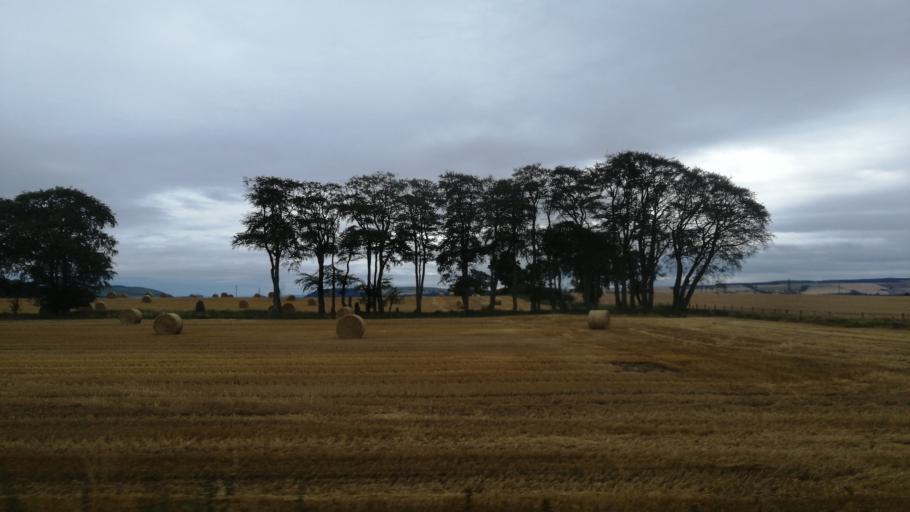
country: GB
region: Scotland
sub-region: Highland
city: Invergordon
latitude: 57.7181
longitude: -4.1206
